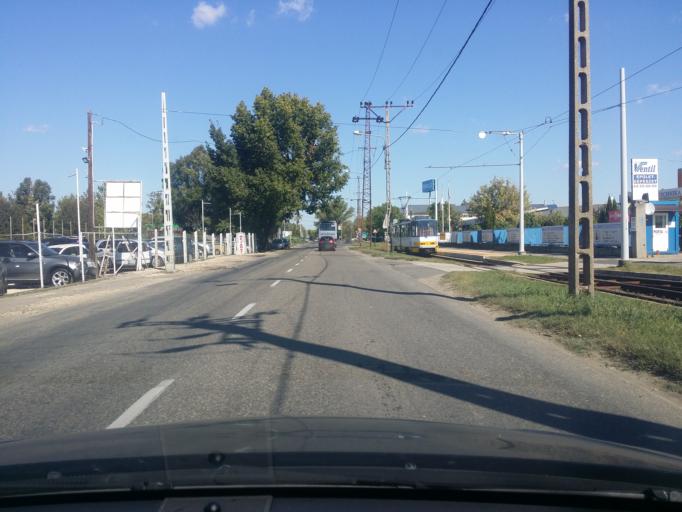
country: HU
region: Csongrad
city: Szeged
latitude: 46.2645
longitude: 20.1099
